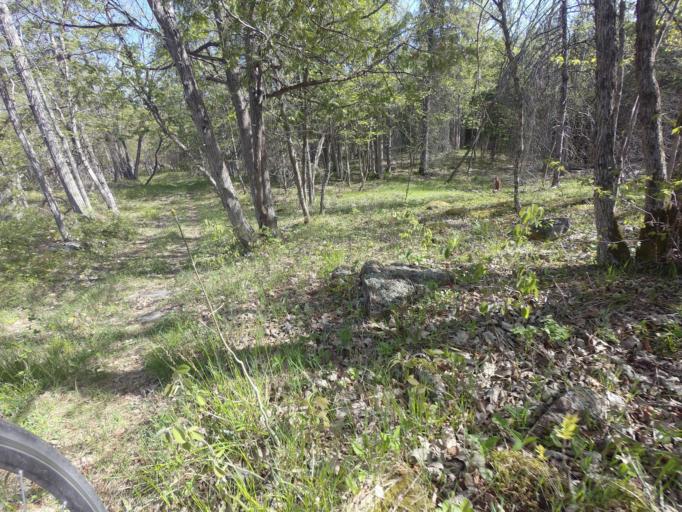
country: CA
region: Ontario
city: Arnprior
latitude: 45.4696
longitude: -76.2996
